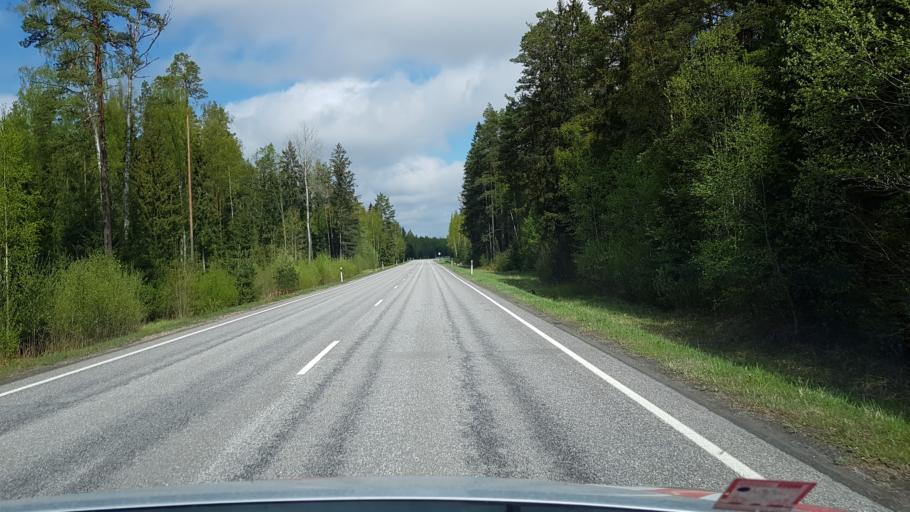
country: EE
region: Paernumaa
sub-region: Saarde vald
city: Kilingi-Nomme
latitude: 58.1870
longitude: 25.0545
